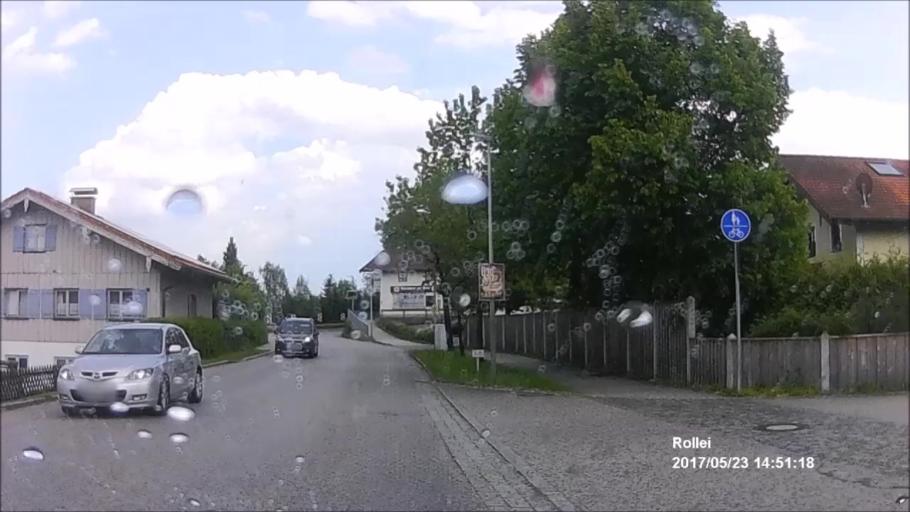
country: DE
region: Bavaria
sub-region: Upper Bavaria
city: Traunreut
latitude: 47.9378
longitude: 12.5918
